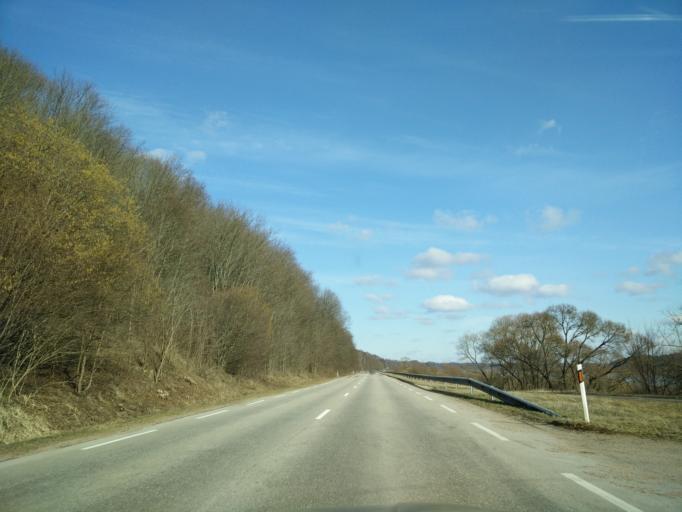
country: LT
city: Gelgaudiskis
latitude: 55.1025
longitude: 23.0130
